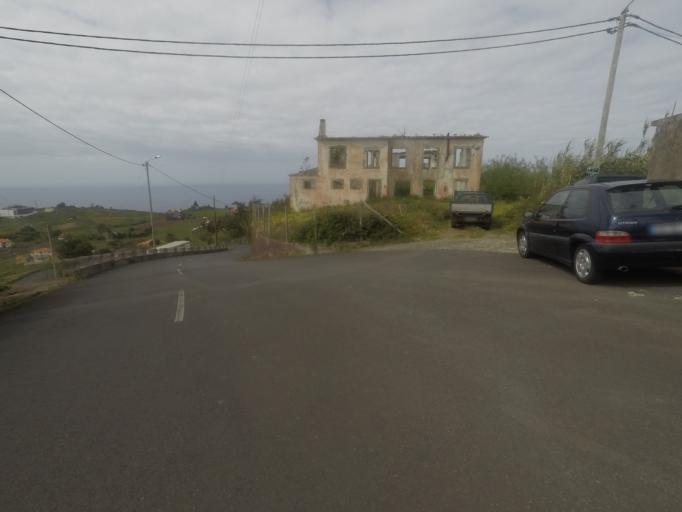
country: PT
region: Madeira
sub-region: Santana
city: Santana
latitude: 32.8203
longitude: -16.8855
